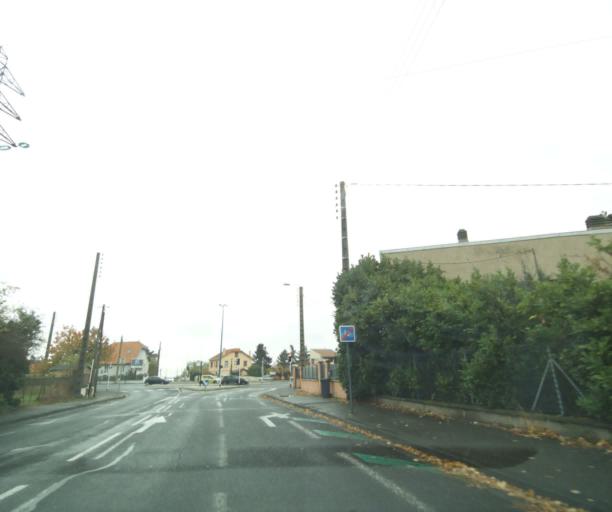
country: FR
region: Auvergne
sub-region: Departement du Puy-de-Dome
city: Aubiere
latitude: 45.7593
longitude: 3.1221
